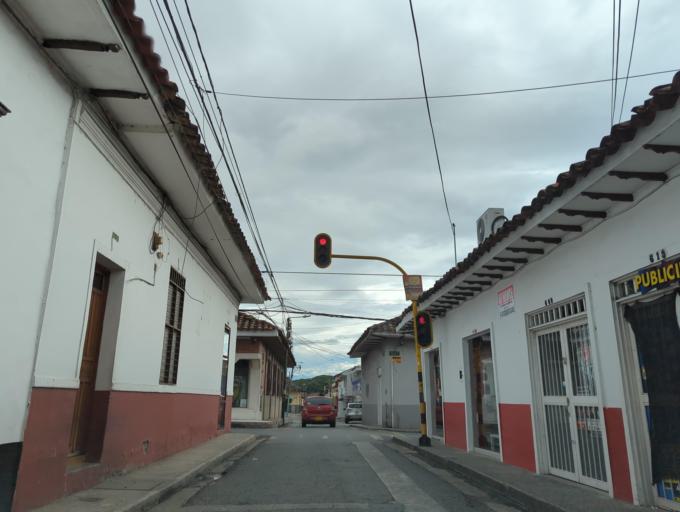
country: CO
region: Valle del Cauca
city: Buga
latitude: 3.8980
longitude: -76.2975
